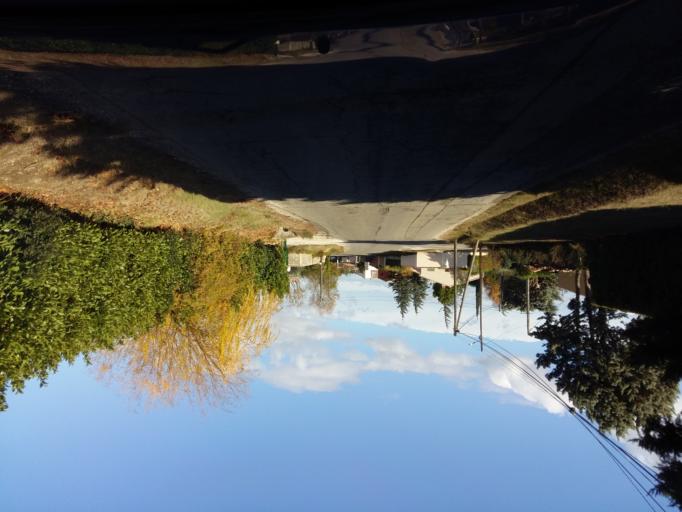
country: FR
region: Provence-Alpes-Cote d'Azur
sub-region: Departement du Vaucluse
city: Camaret-sur-Aigues
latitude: 44.1694
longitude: 4.8658
